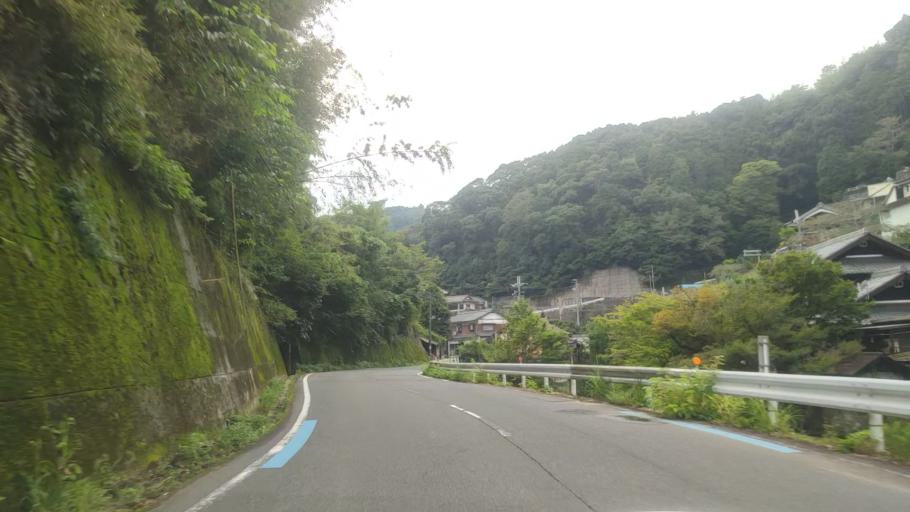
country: JP
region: Wakayama
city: Hashimoto
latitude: 34.2729
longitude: 135.5680
